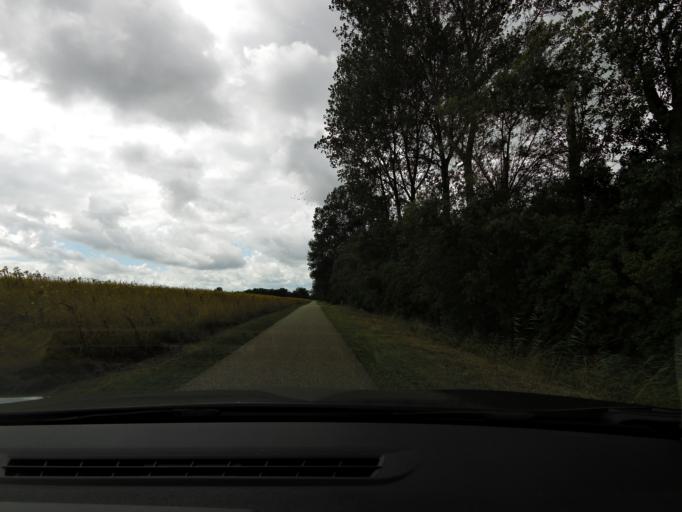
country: NL
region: South Holland
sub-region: Gemeente Goeree-Overflakkee
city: Goedereede
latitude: 51.8321
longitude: 3.9964
